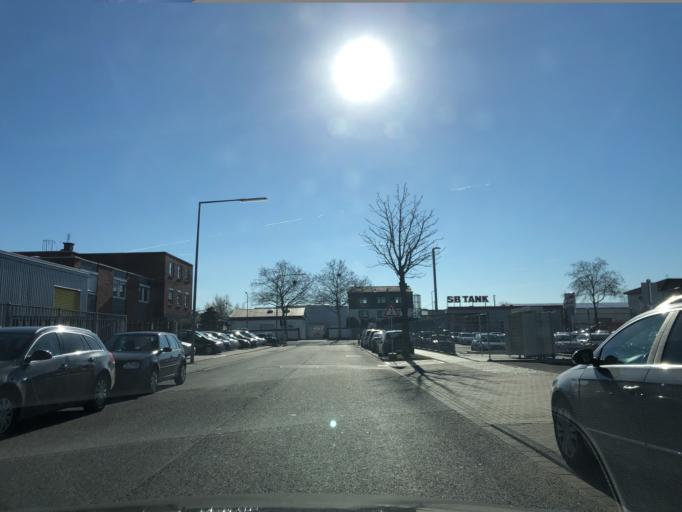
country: DE
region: North Rhine-Westphalia
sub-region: Regierungsbezirk Koln
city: Wahn-Heide
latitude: 50.8416
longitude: 7.1024
